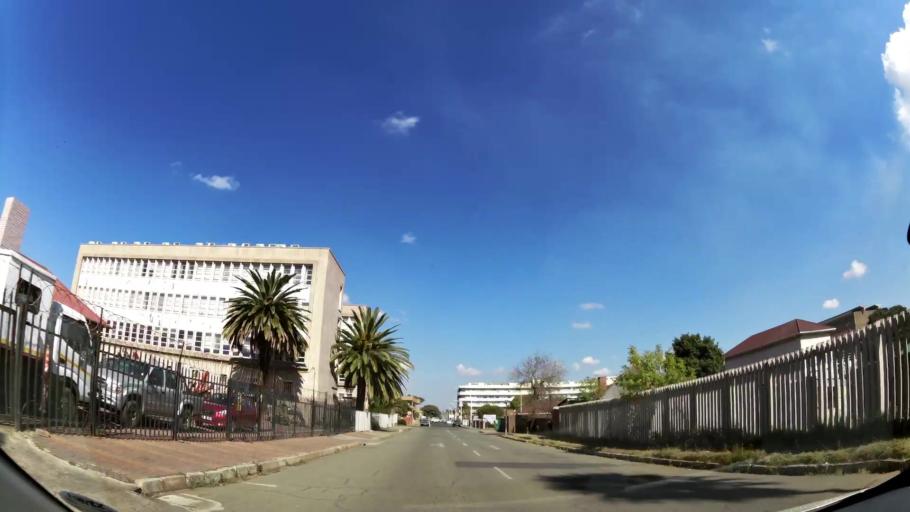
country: ZA
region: Mpumalanga
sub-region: Nkangala District Municipality
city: Witbank
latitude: -25.8731
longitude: 29.2174
